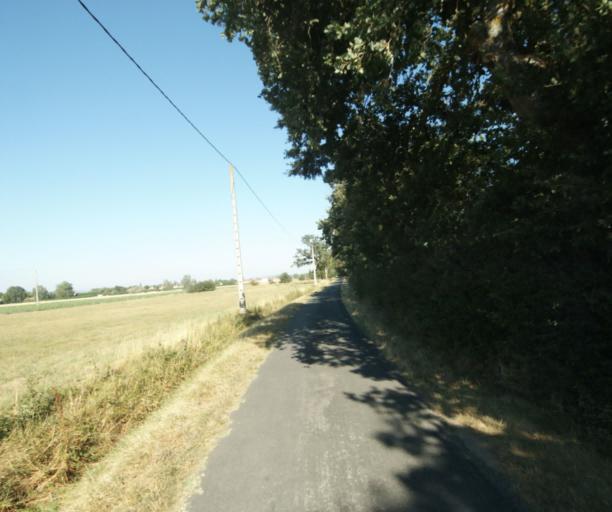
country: FR
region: Midi-Pyrenees
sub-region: Departement de la Haute-Garonne
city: Revel
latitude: 43.4620
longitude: 2.0241
